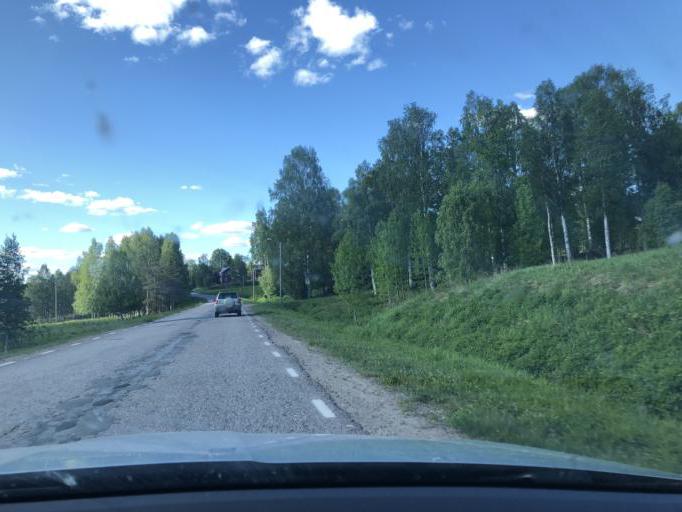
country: SE
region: Norrbotten
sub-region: Kalix Kommun
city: Kalix
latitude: 65.9972
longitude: 23.1459
